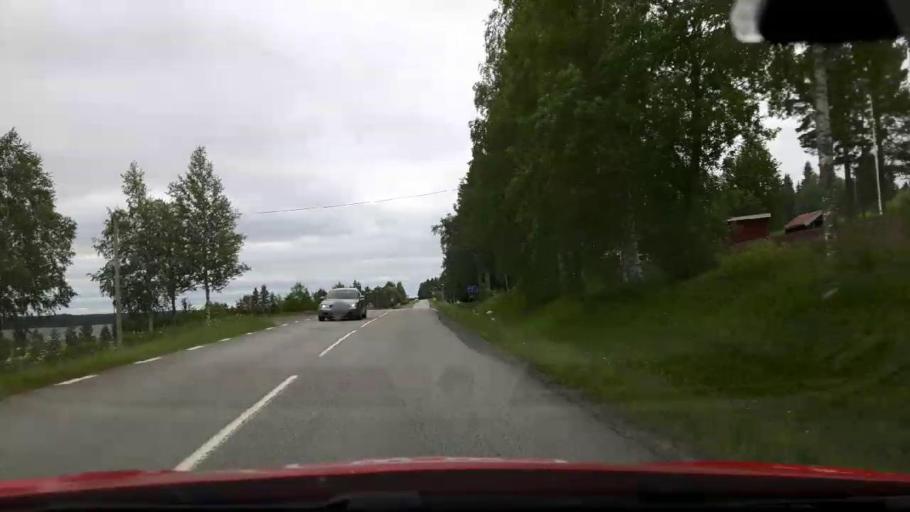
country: SE
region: Jaemtland
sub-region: Stroemsunds Kommun
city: Stroemsund
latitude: 63.5657
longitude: 15.3937
